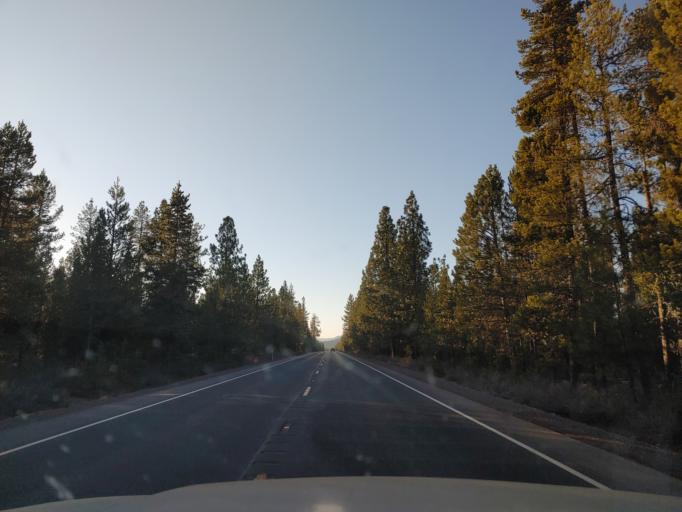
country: US
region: Oregon
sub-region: Deschutes County
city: La Pine
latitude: 43.3905
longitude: -121.8112
